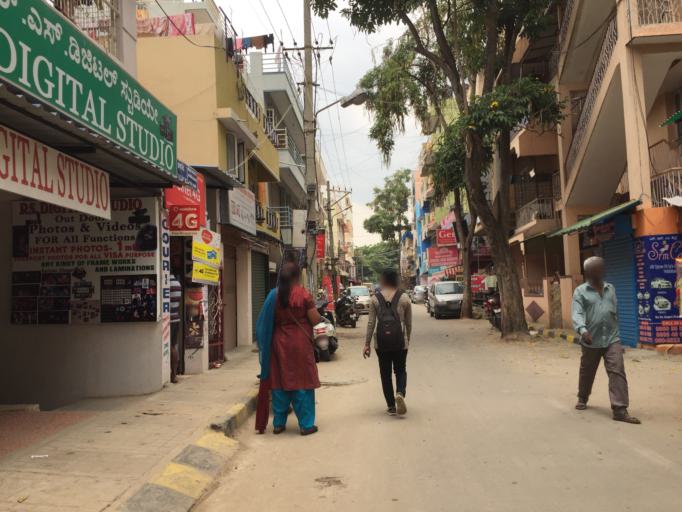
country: IN
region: Karnataka
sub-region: Bangalore Urban
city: Bangalore
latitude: 12.9579
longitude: 77.6595
